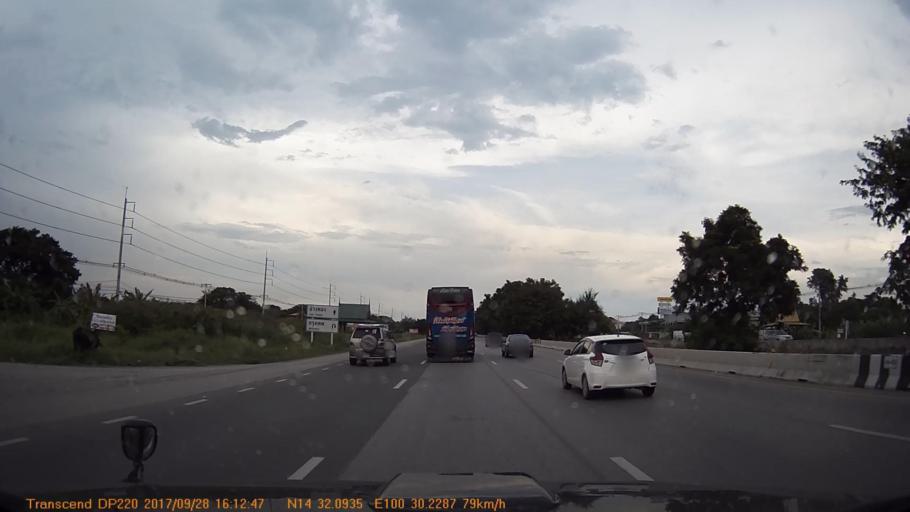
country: TH
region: Phra Nakhon Si Ayutthaya
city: Maha Rat
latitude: 14.5359
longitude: 100.5035
